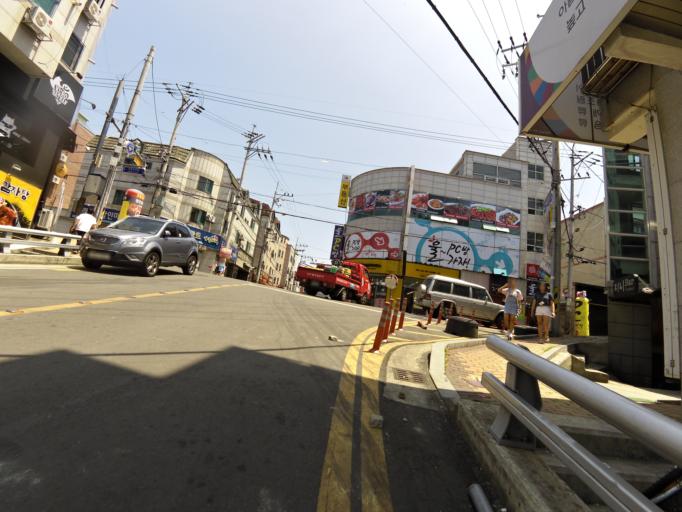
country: KR
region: Gyeongsangbuk-do
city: Gyeongsan-si
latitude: 35.8385
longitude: 128.7529
